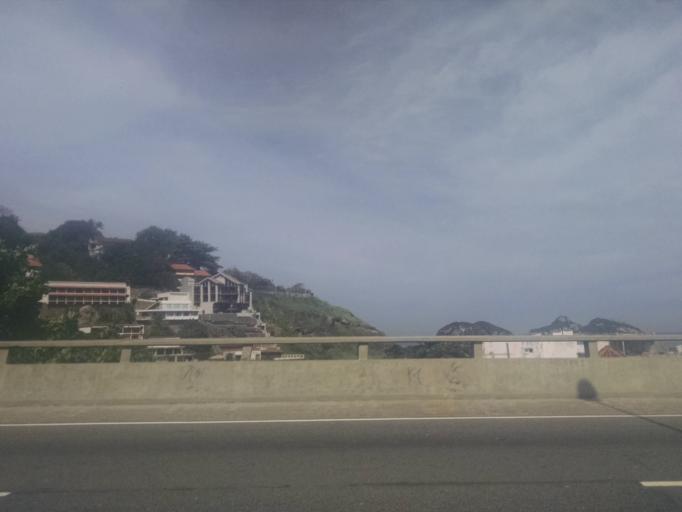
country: BR
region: Rio de Janeiro
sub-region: Rio De Janeiro
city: Rio de Janeiro
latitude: -23.0128
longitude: -43.2941
